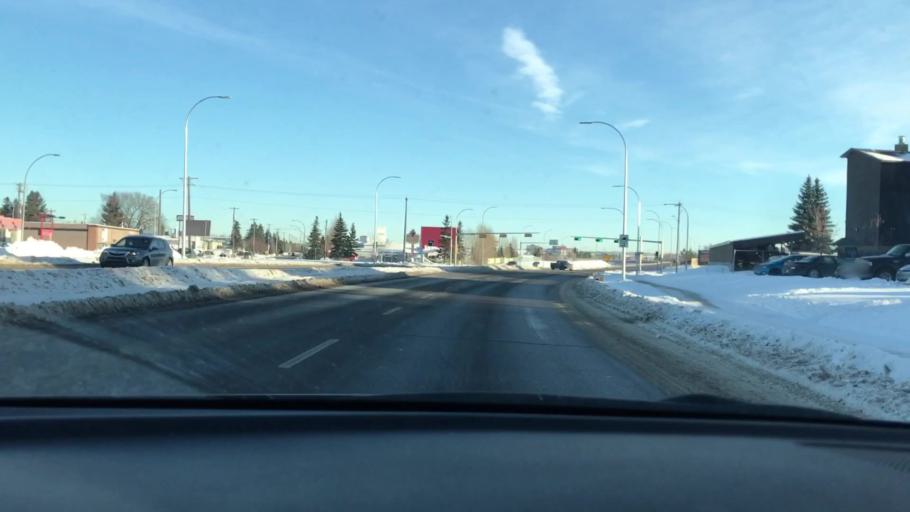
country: CA
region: Alberta
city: Edmonton
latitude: 53.5179
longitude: -113.4389
